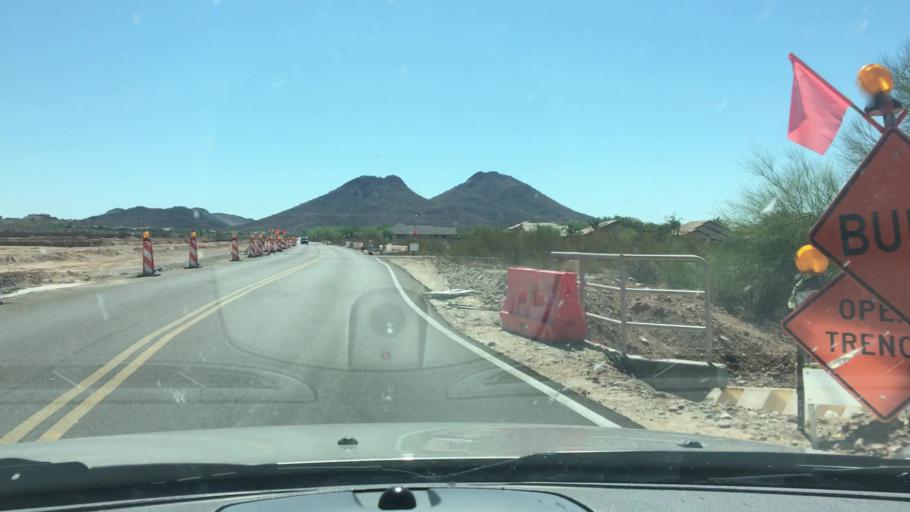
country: US
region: Arizona
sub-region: Maricopa County
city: Sun City West
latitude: 33.7250
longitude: -112.2198
